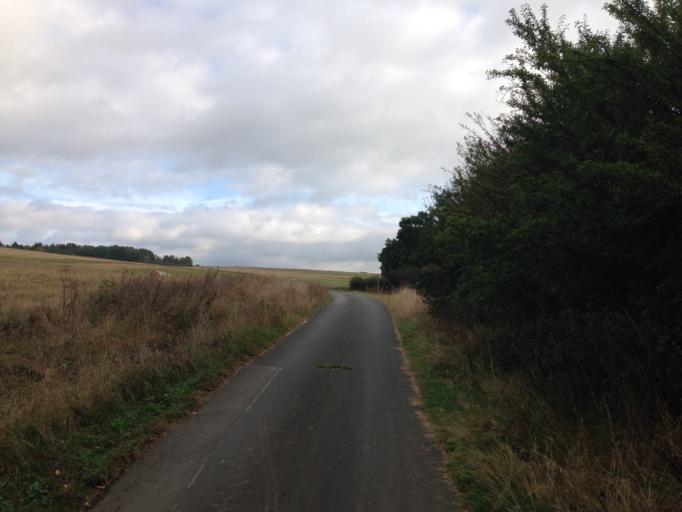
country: DE
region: Hesse
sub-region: Regierungsbezirk Giessen
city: Lohra
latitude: 50.6594
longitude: 8.5682
